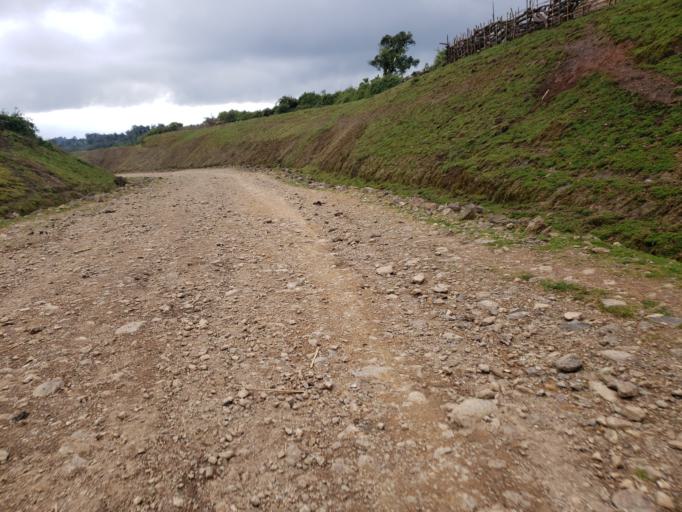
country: ET
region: Oromiya
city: Dodola
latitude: 6.6987
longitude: 39.3710
